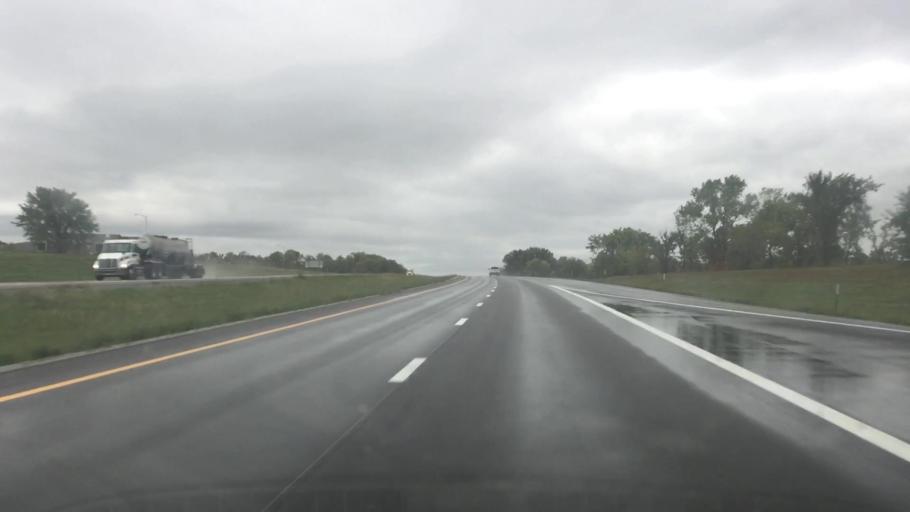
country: US
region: Kansas
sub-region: Johnson County
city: Spring Hill
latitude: 38.7217
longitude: -94.8347
